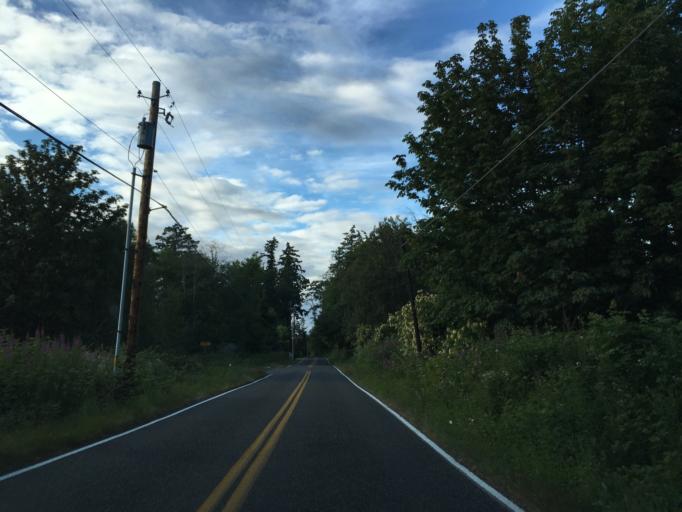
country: CA
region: British Columbia
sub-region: Greater Vancouver Regional District
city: White Rock
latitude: 48.9611
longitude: -122.8050
